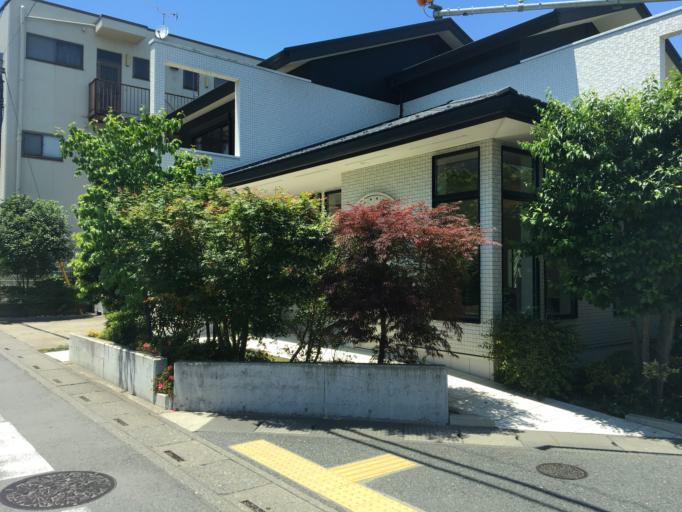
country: JP
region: Saitama
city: Sakado
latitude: 35.9461
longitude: 139.4067
